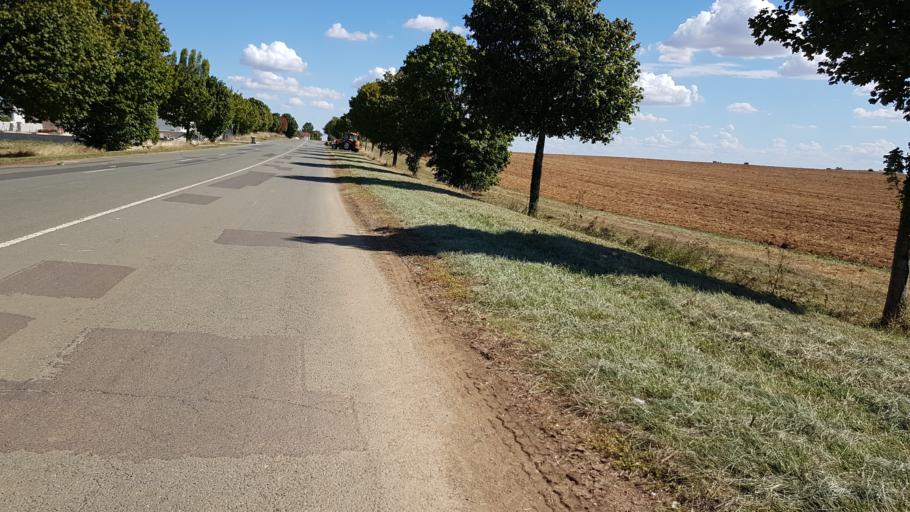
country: FR
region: Poitou-Charentes
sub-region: Departement des Deux-Sevres
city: Vouille
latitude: 46.3150
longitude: -0.3821
